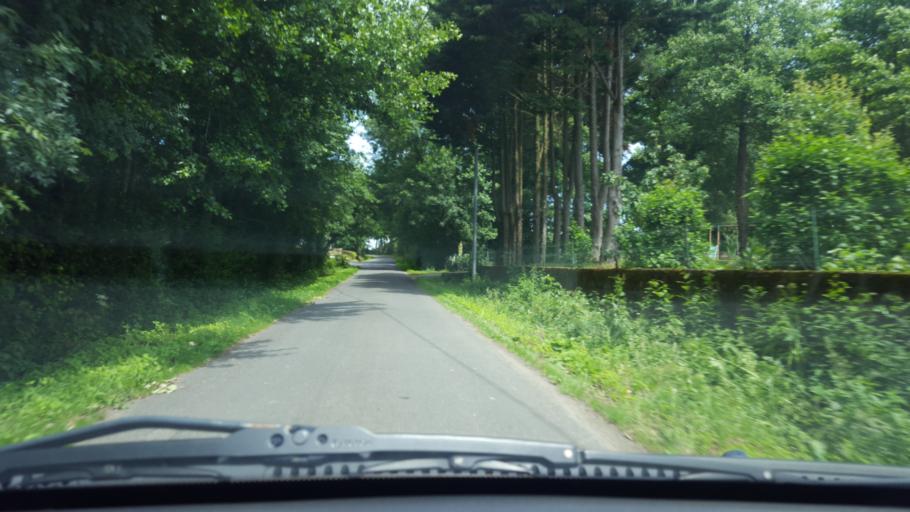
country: FR
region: Pays de la Loire
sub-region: Departement de la Loire-Atlantique
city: La Limouziniere
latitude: 47.0392
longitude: -1.5808
